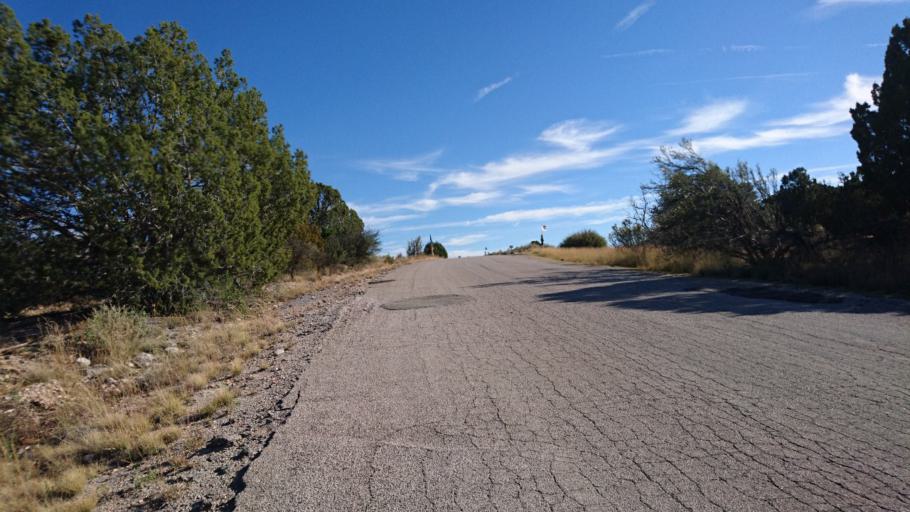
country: US
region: Arizona
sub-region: Mohave County
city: Peach Springs
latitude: 35.5201
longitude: -113.2250
